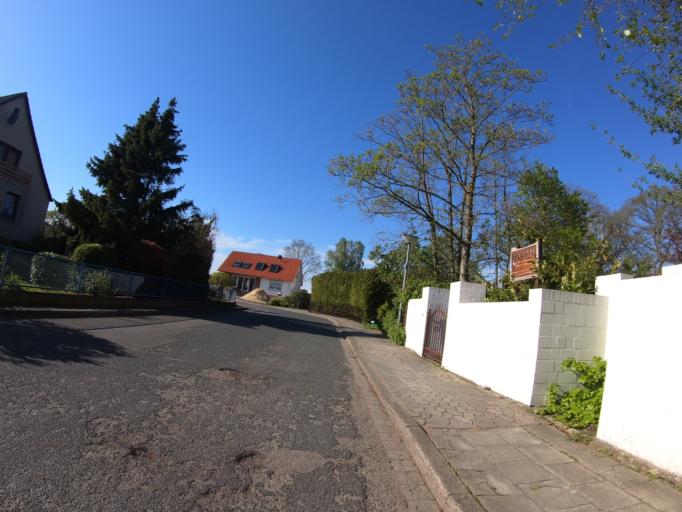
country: DE
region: Lower Saxony
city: Meine
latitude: 52.3903
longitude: 10.5419
